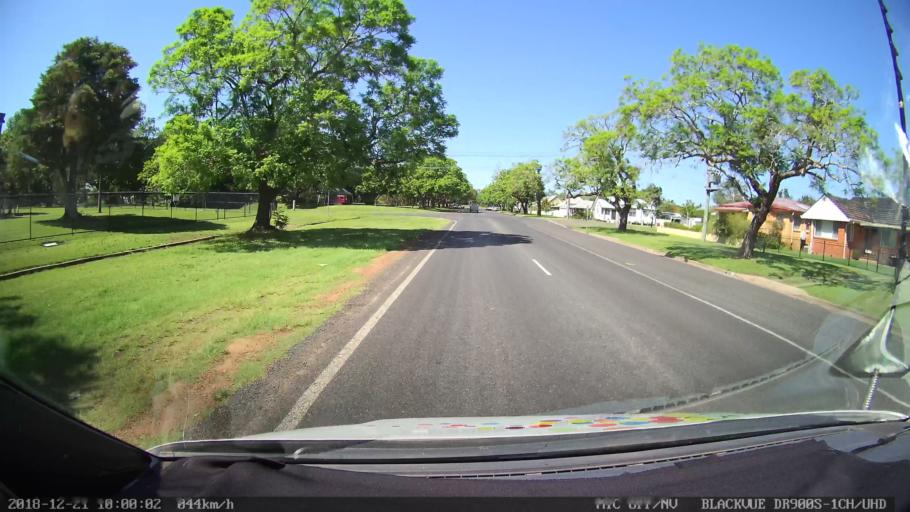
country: AU
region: New South Wales
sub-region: Clarence Valley
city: Grafton
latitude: -29.6818
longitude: 152.9279
